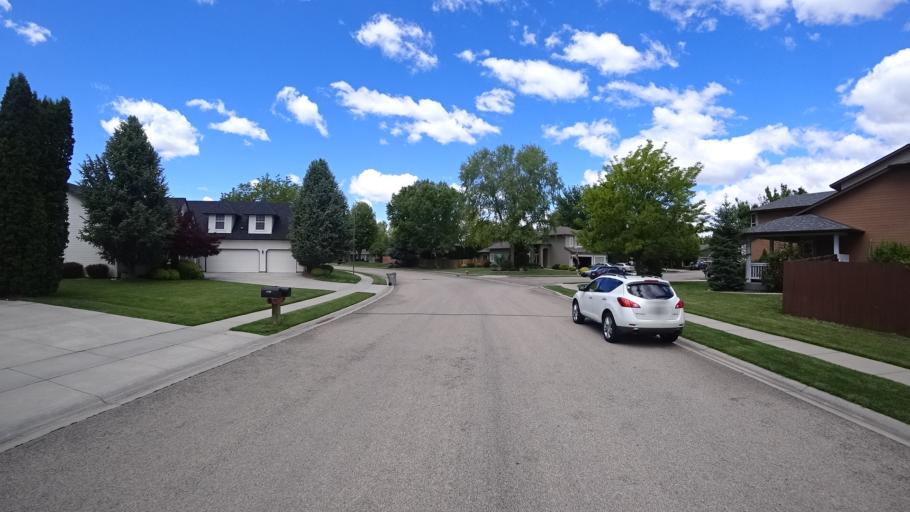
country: US
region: Idaho
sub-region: Ada County
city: Eagle
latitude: 43.6522
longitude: -116.3462
